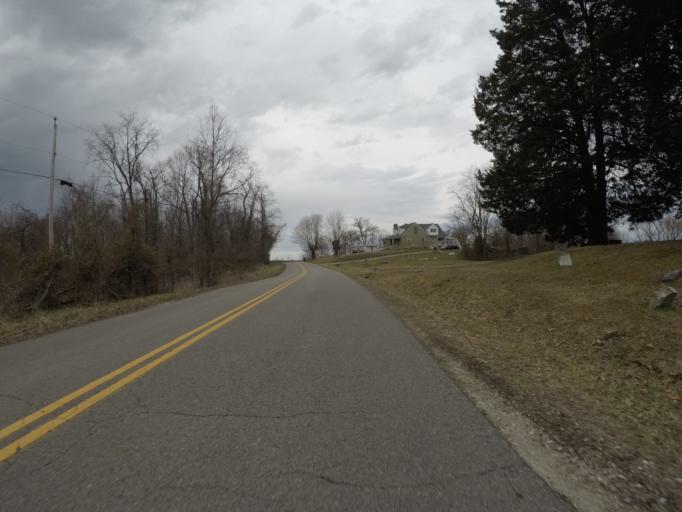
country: US
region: Ohio
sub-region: Lawrence County
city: Burlington
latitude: 38.4422
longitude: -82.5248
